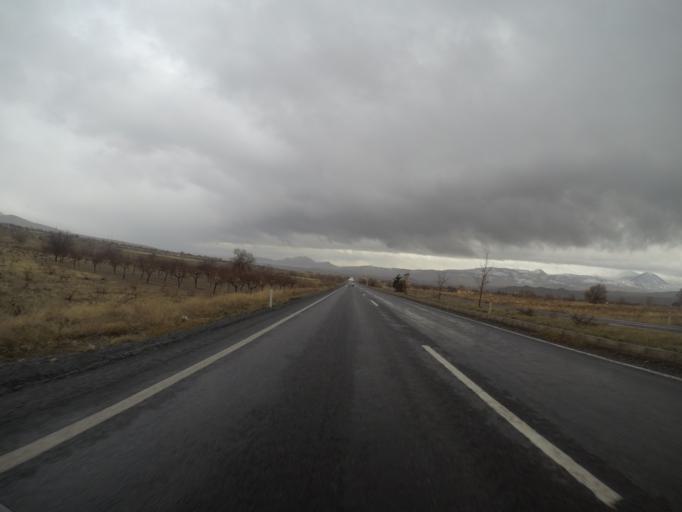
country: TR
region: Kayseri
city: Incesu
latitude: 38.6811
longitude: 35.2091
